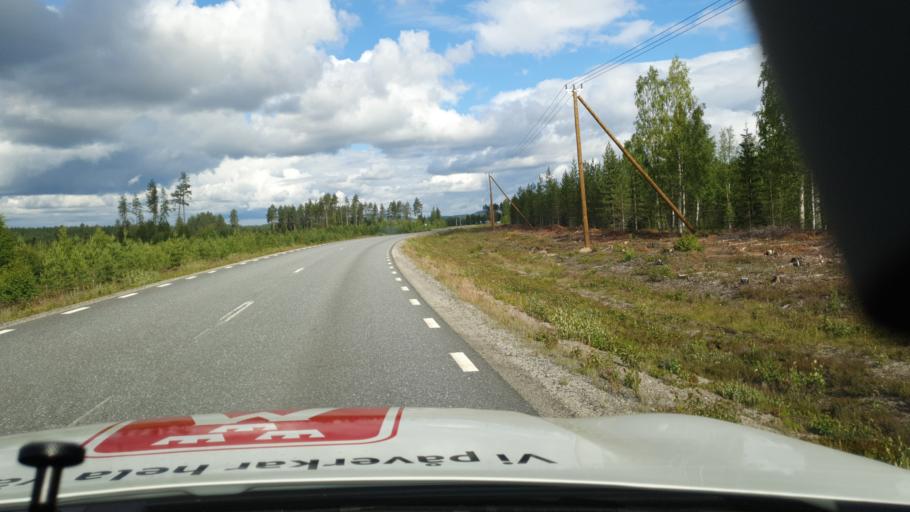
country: SE
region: Vaesterbotten
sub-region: Bjurholms Kommun
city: Bjurholm
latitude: 64.2951
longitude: 19.1810
